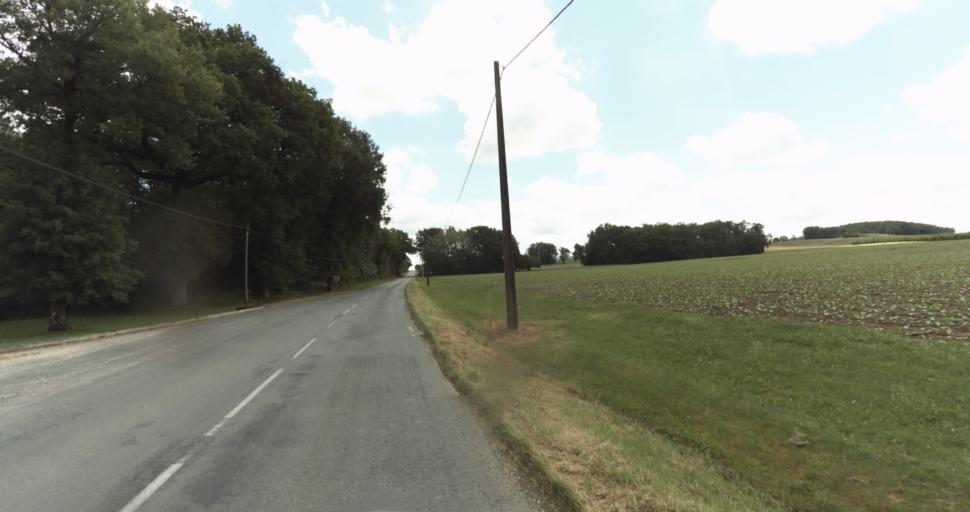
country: FR
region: Aquitaine
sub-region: Departement de la Dordogne
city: Beaumont-du-Perigord
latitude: 44.7315
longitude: 0.7883
